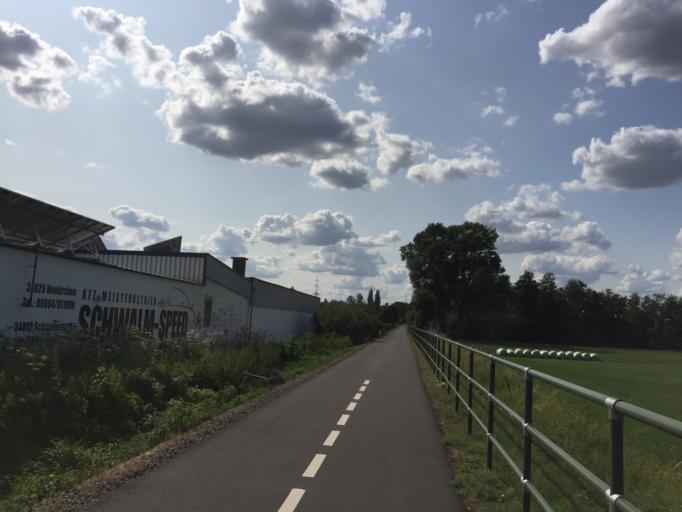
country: DE
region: Hesse
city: Schwalmstadt
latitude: 50.9053
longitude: 9.2216
